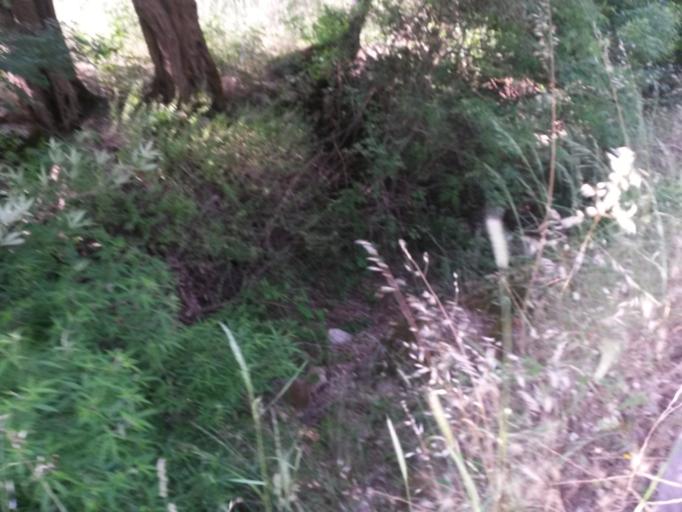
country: GR
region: North Aegean
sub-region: Nomos Lesvou
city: Agiasos
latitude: 39.1141
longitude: 26.3890
